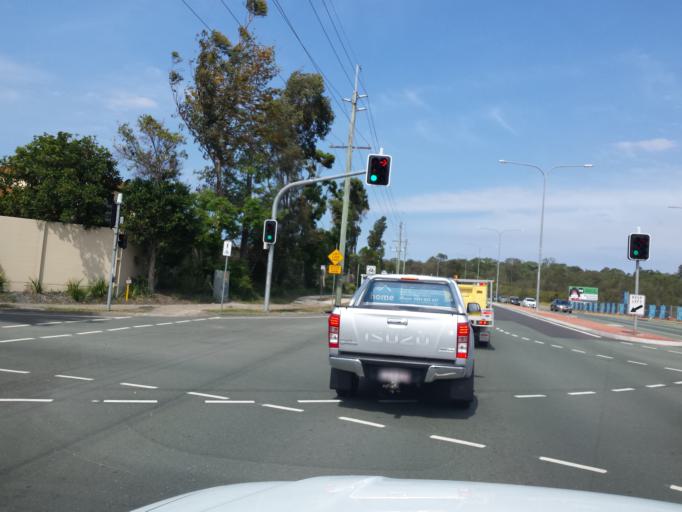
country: AU
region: Queensland
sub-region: Gold Coast
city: Oxenford
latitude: -27.8855
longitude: 153.3190
